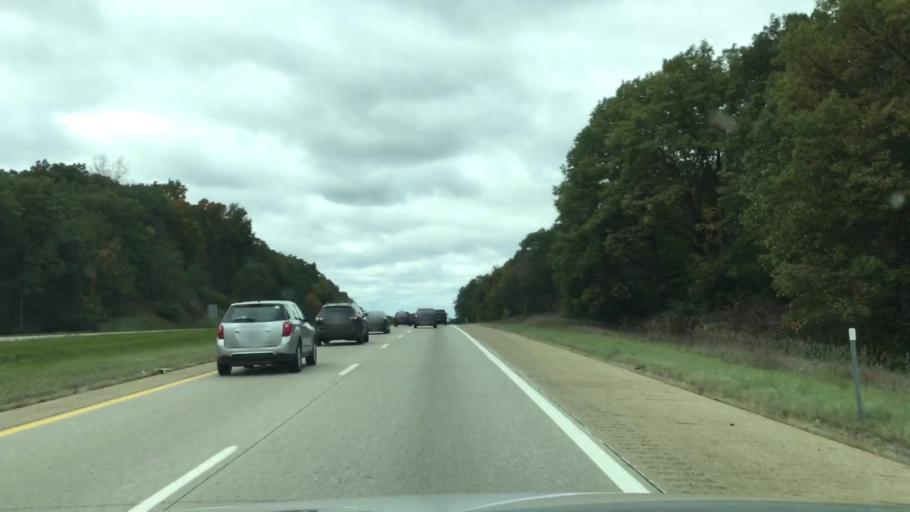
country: US
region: Michigan
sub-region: Calhoun County
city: Albion
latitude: 42.2622
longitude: -84.6828
